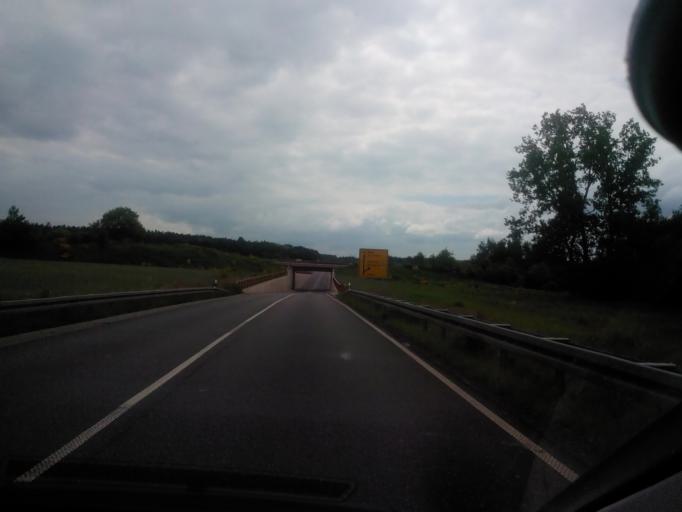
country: DE
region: Saarland
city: Uberherrn
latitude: 49.2476
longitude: 6.7170
